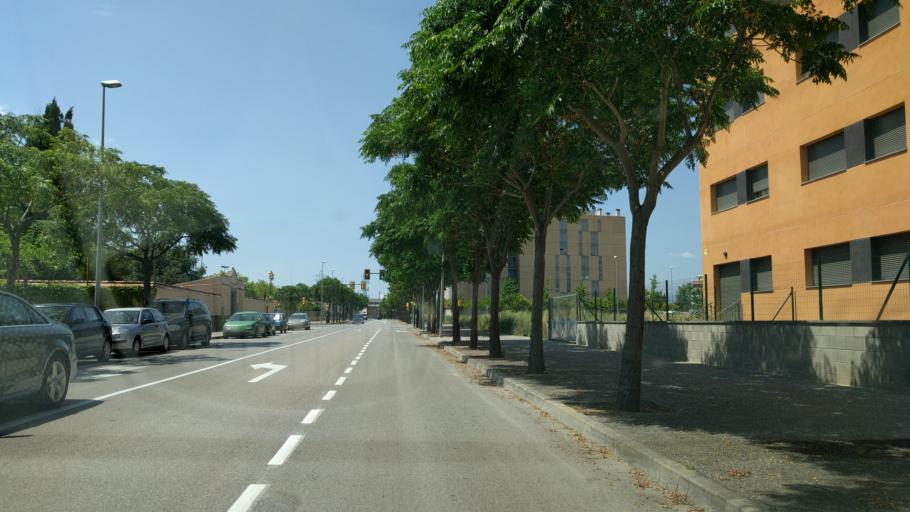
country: ES
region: Catalonia
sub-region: Provincia de Girona
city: Salt
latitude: 41.9723
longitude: 2.8040
